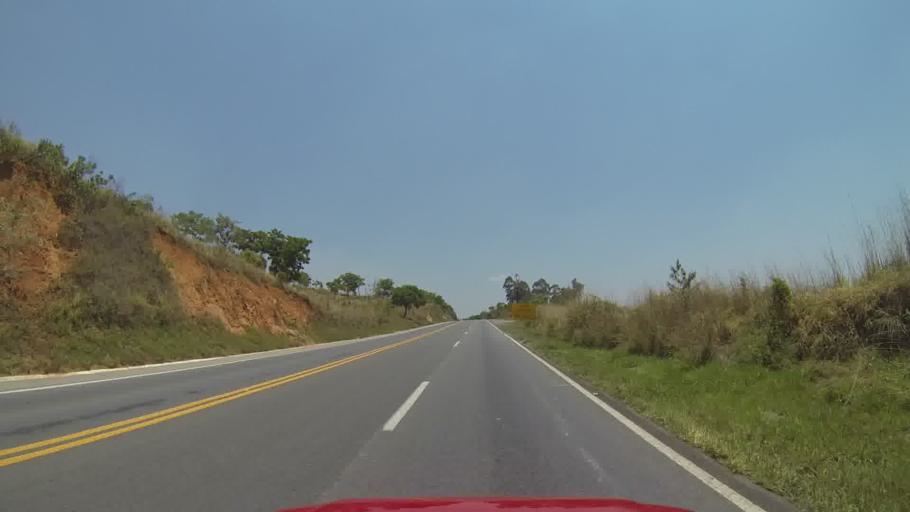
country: BR
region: Minas Gerais
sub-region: Itapecerica
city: Itapecerica
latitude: -20.3003
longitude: -45.1998
